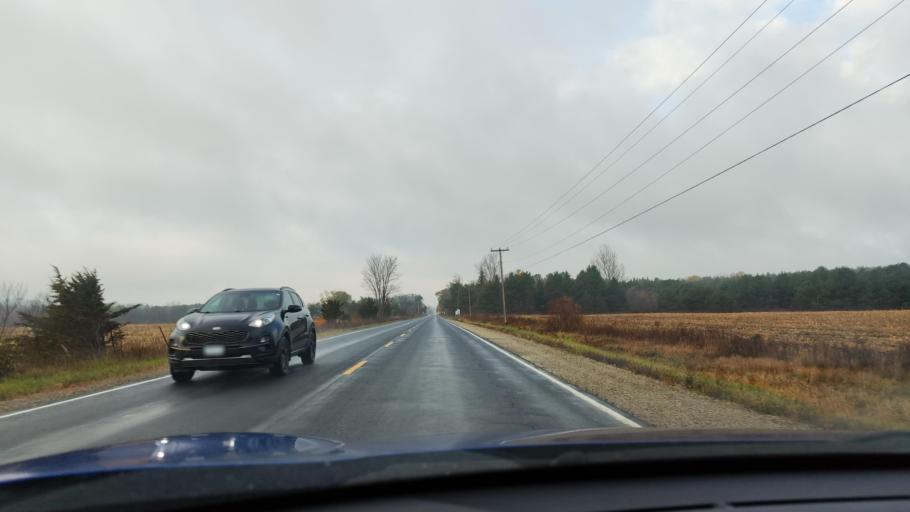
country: CA
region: Ontario
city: Angus
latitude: 44.3613
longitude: -79.9586
